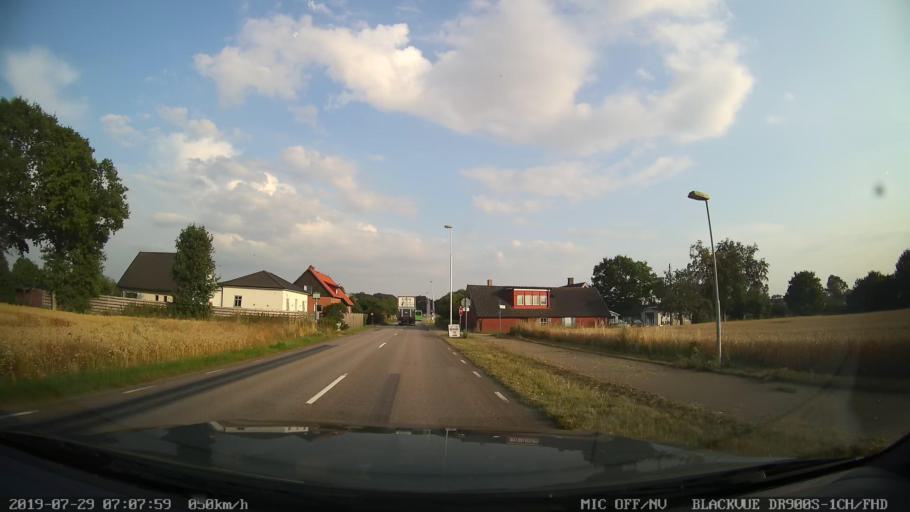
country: SE
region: Skane
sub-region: Helsingborg
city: Odakra
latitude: 56.1033
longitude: 12.6963
